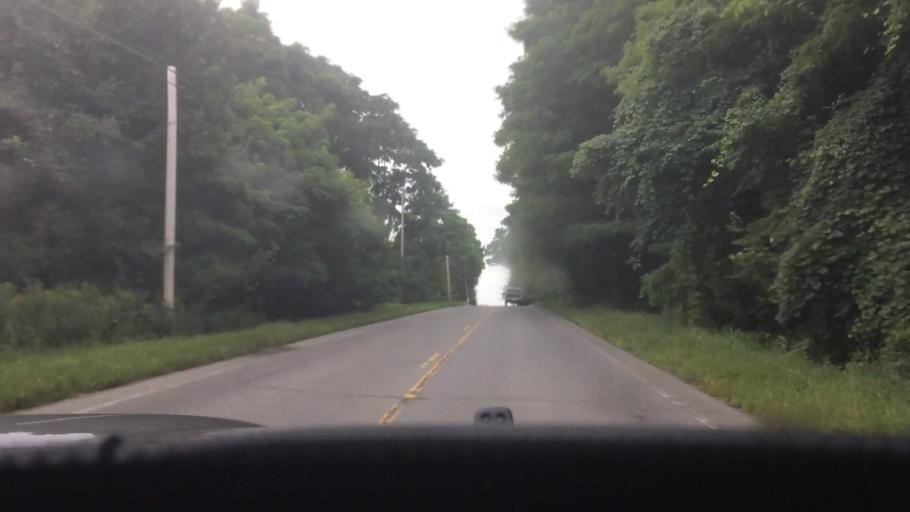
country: US
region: New York
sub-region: St. Lawrence County
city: Canton
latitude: 44.4953
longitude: -75.2164
